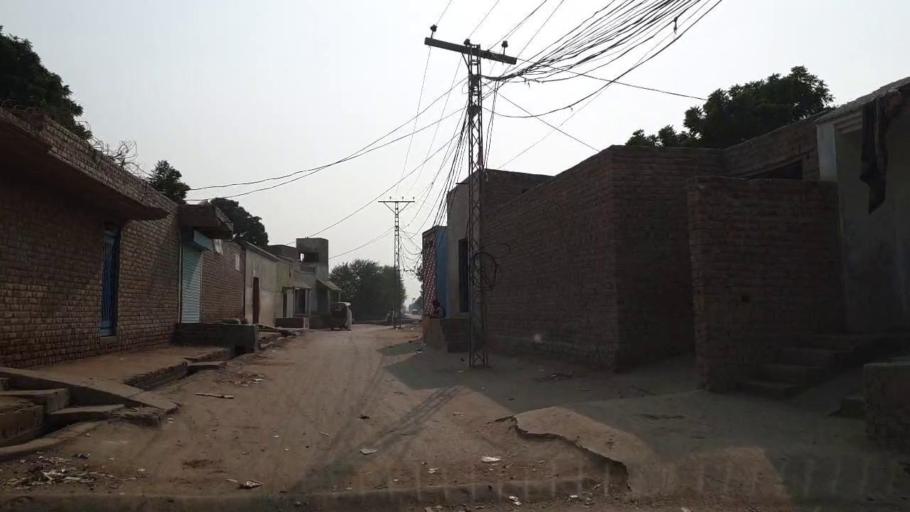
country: PK
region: Sindh
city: Bhan
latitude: 26.5784
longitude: 67.7296
